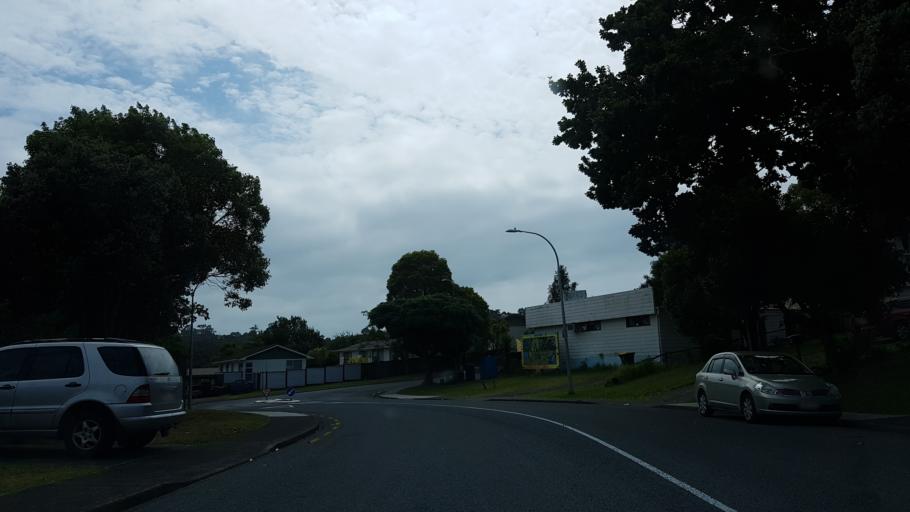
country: NZ
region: Auckland
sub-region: Auckland
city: North Shore
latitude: -36.7718
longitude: 174.7046
